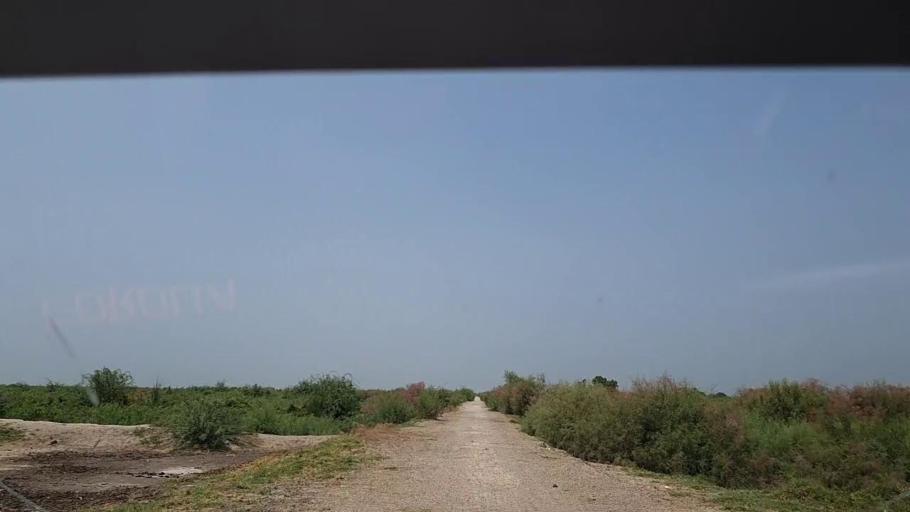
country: PK
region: Sindh
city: Adilpur
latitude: 27.8929
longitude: 69.2467
